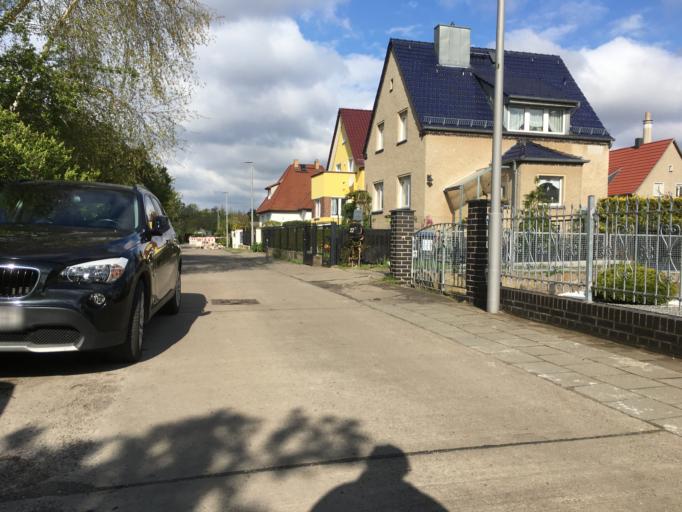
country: DE
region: Berlin
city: Biesdorf
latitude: 52.5147
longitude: 13.5313
